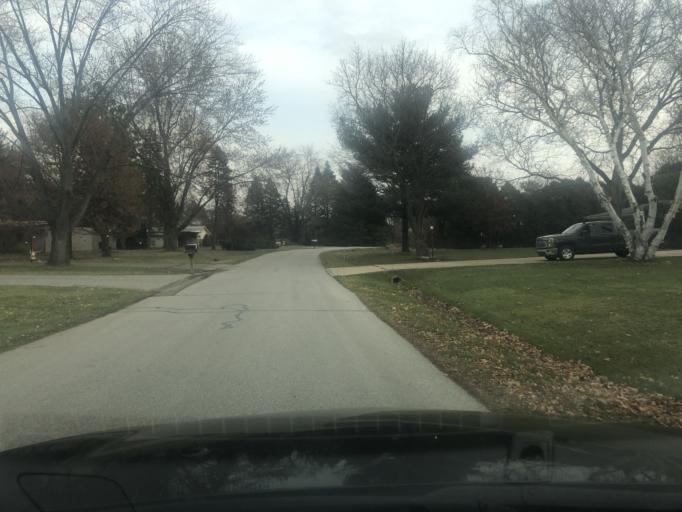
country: US
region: Michigan
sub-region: Wayne County
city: Belleville
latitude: 42.2148
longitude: -83.4842
